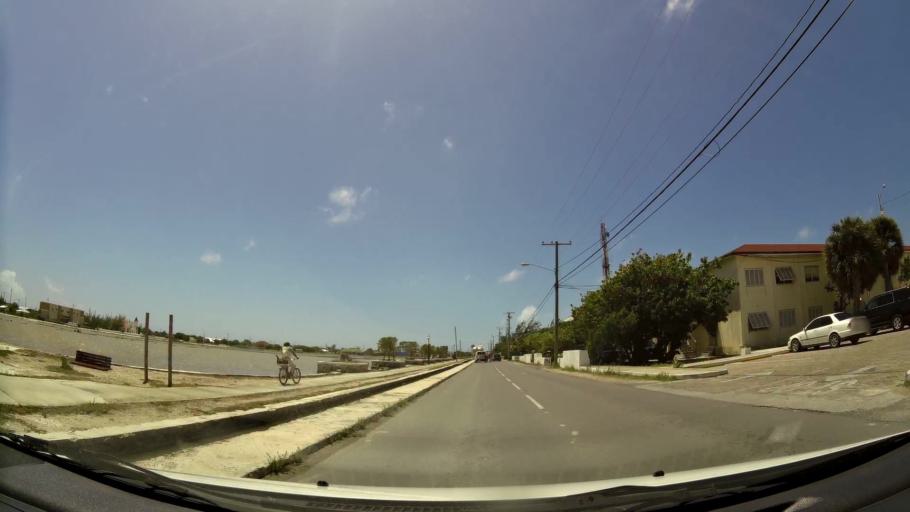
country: TC
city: Cockburn Town
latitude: 21.4666
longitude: -71.1458
